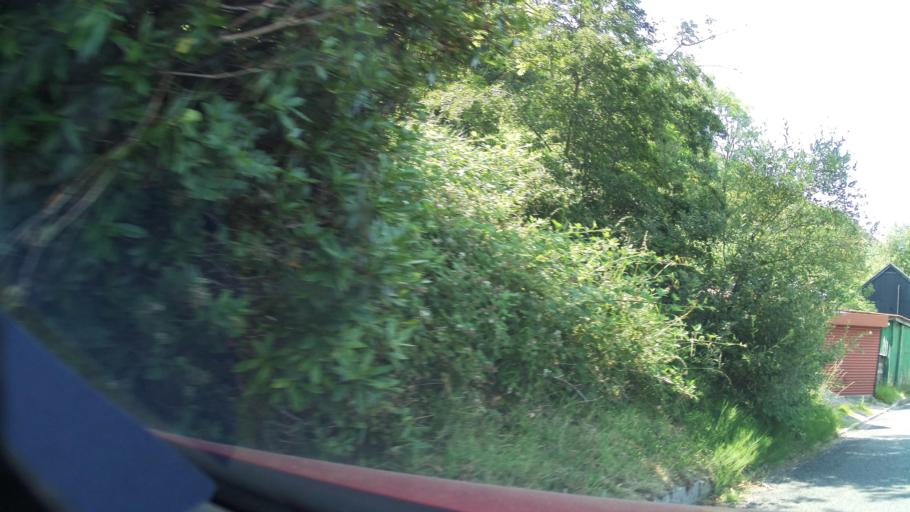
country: GB
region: Wales
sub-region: Caerphilly County Borough
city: New Tredegar
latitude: 51.7175
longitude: -3.2438
